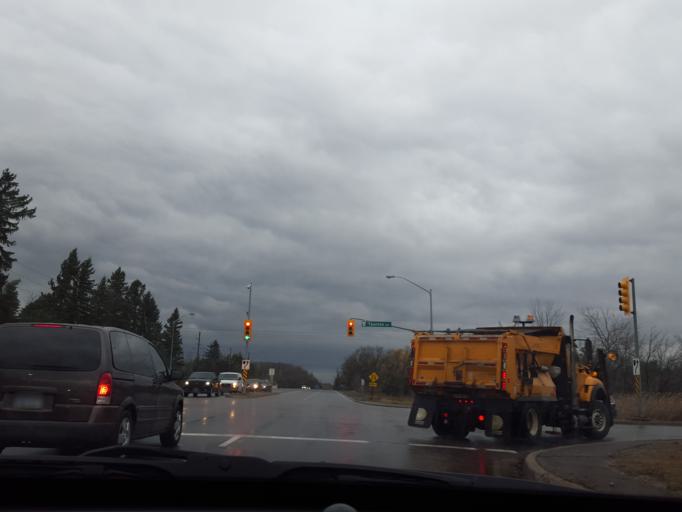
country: CA
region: Ontario
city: Pickering
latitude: 43.8868
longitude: -79.0908
